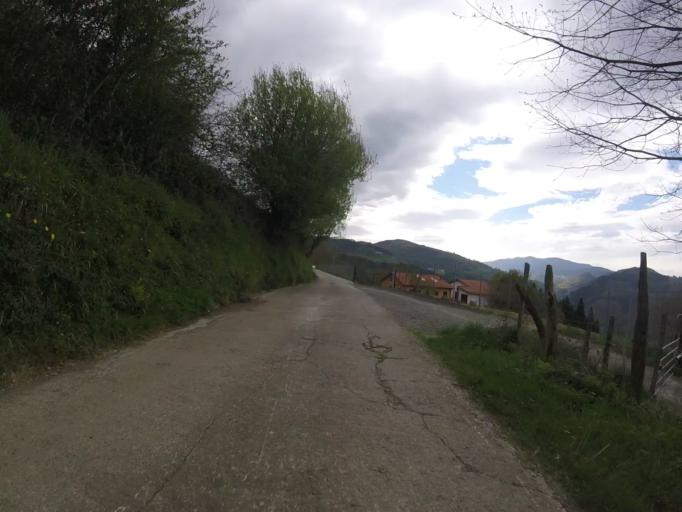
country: ES
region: Basque Country
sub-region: Provincia de Guipuzcoa
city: Aizarnazabal
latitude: 43.2530
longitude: -2.2131
